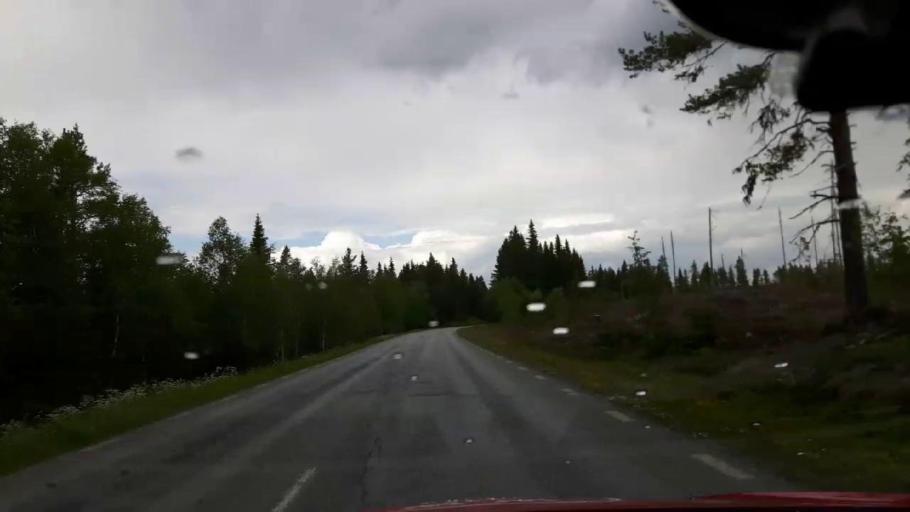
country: SE
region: Jaemtland
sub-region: Krokoms Kommun
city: Krokom
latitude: 63.4205
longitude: 14.2242
